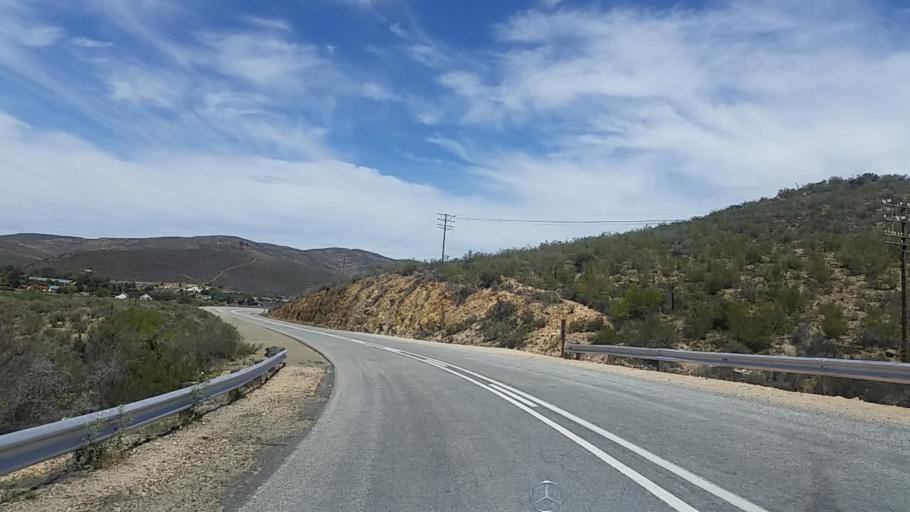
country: ZA
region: Western Cape
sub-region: Eden District Municipality
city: Knysna
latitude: -33.6431
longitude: 23.1331
